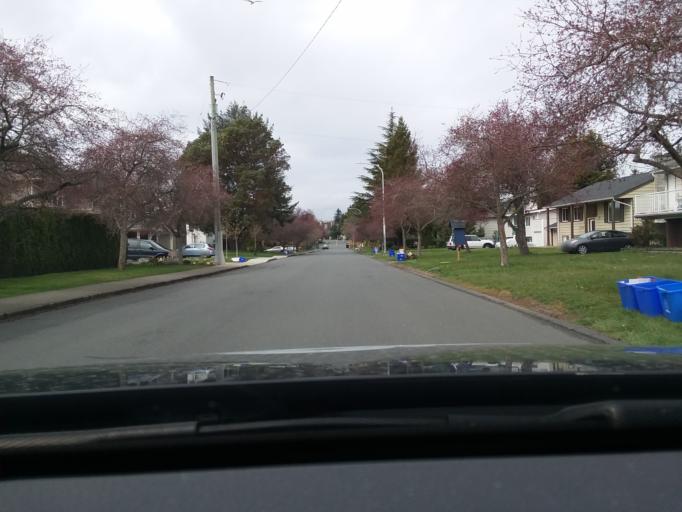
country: CA
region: British Columbia
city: Oak Bay
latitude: 48.4728
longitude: -123.3282
